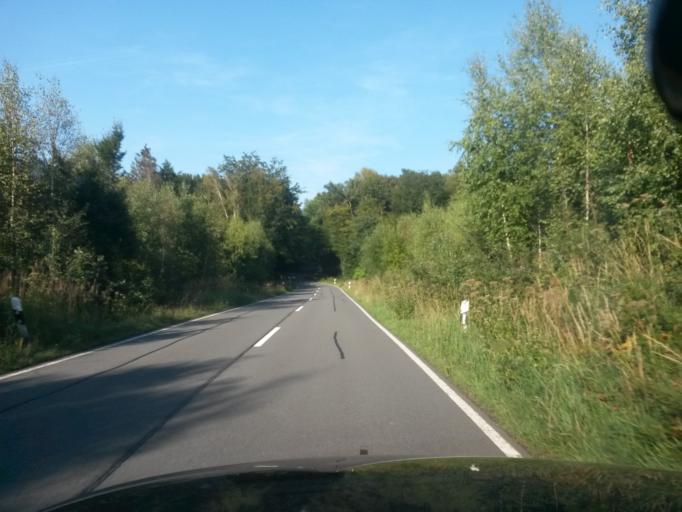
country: DE
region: North Rhine-Westphalia
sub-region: Regierungsbezirk Koln
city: Ruppichteroth
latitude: 50.8845
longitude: 7.5052
